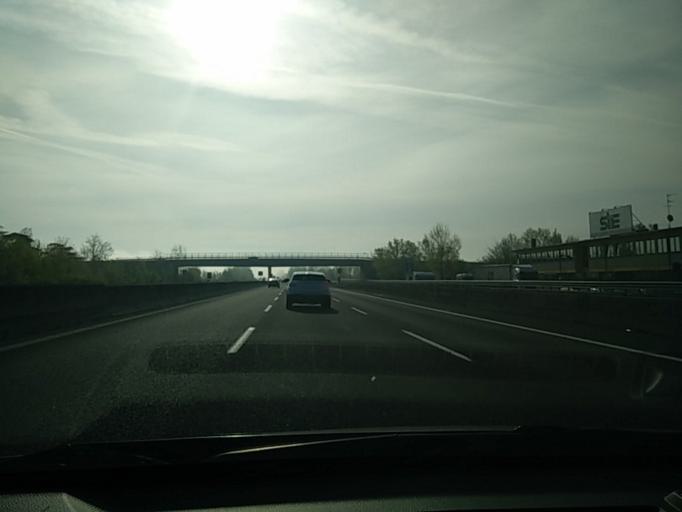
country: IT
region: Emilia-Romagna
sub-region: Provincia di Bologna
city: Ozzano dell'Emilia
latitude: 44.4616
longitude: 11.5012
